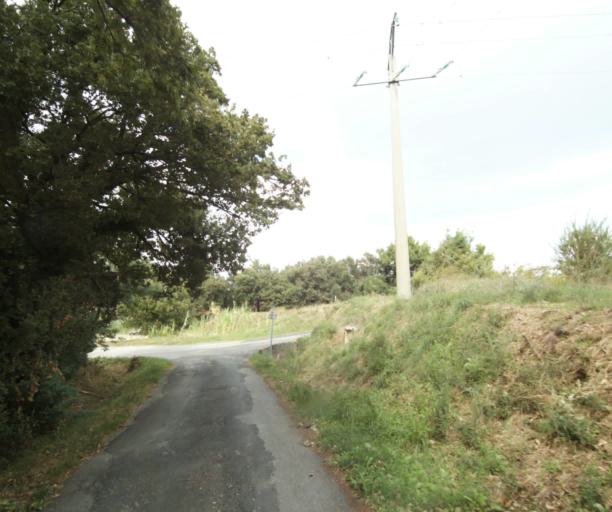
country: FR
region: Languedoc-Roussillon
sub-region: Departement des Pyrenees-Orientales
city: Argelers
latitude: 42.5403
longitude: 3.0185
